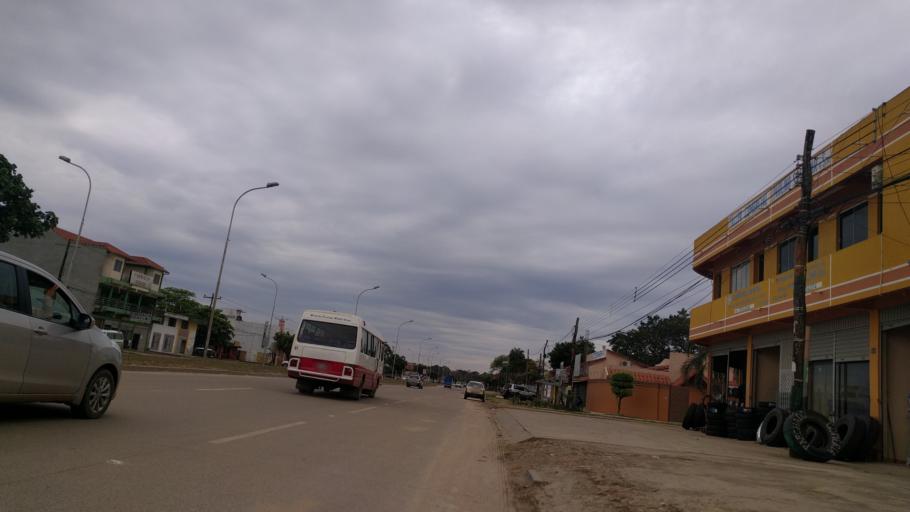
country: BO
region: Santa Cruz
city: Santa Cruz de la Sierra
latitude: -17.8376
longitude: -63.1822
